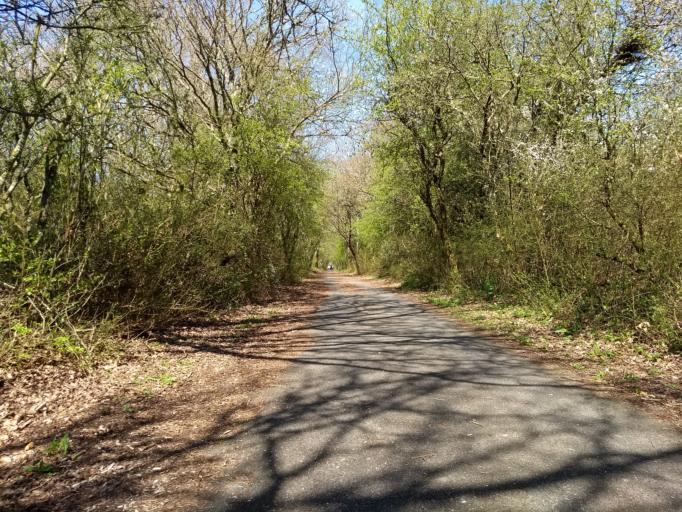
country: GB
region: England
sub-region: Isle of Wight
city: East Cowes
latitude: 50.7396
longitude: -1.2908
